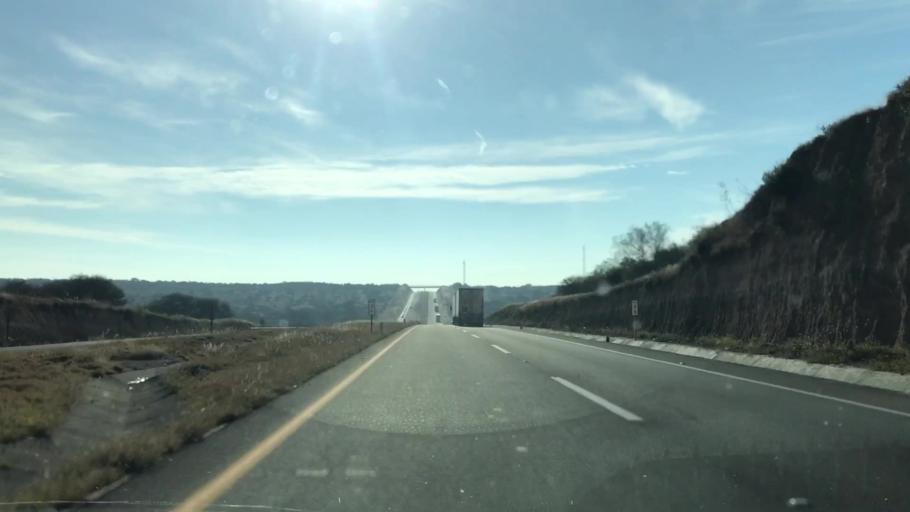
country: MX
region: Jalisco
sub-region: Union de San Antonio
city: San Jose del Caliche (El Caliche)
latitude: 21.1958
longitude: -101.8964
